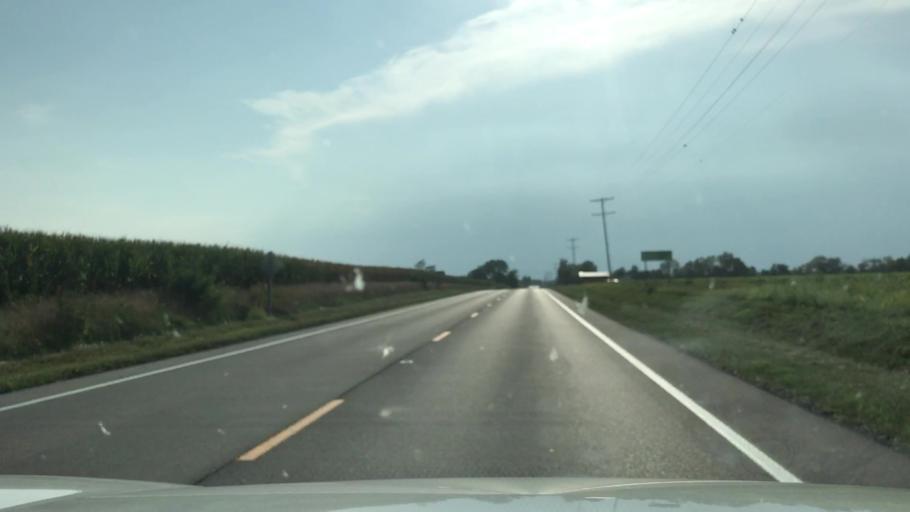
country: US
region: Illinois
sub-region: Washington County
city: Nashville
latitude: 38.4417
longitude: -89.3730
